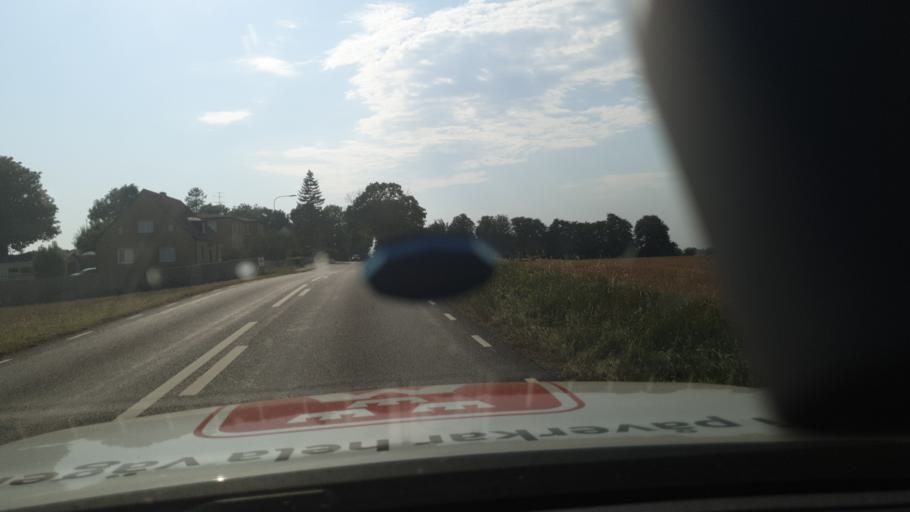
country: SE
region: Skane
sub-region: Svedala Kommun
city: Svedala
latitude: 55.4540
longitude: 13.2190
